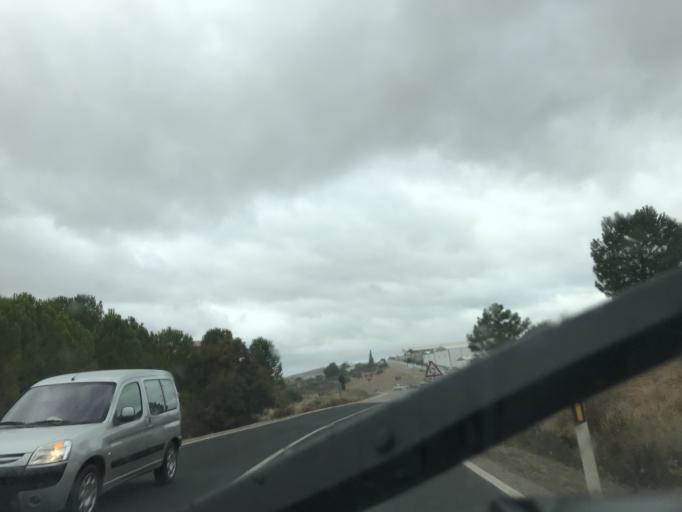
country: ES
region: Andalusia
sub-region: Provincia de Jaen
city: Peal de Becerro
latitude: 37.9179
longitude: -3.1302
